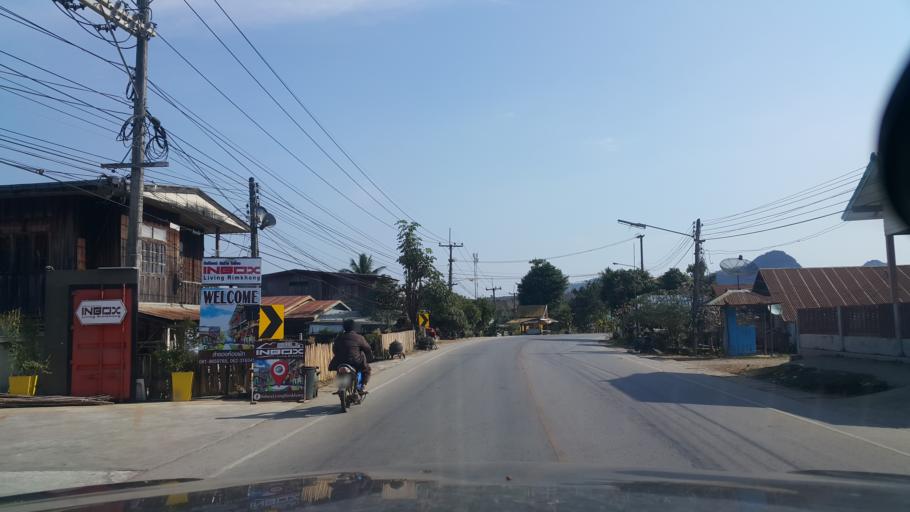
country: LA
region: Vientiane
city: Muang Sanakham
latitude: 17.9052
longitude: 101.7220
